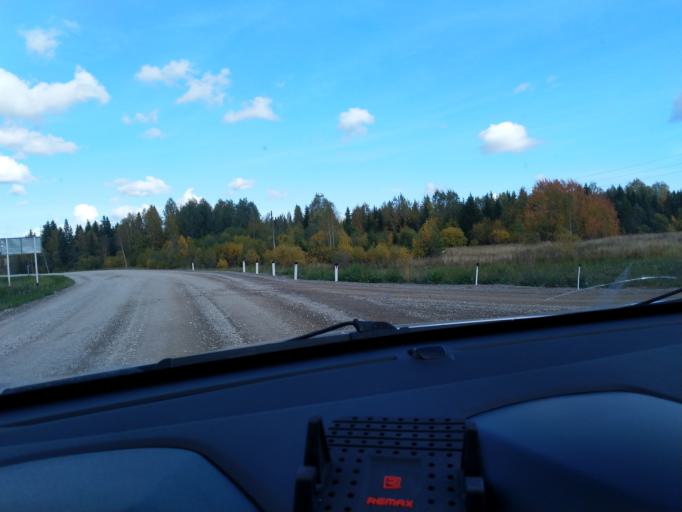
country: RU
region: Perm
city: Usol'ye
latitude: 59.4639
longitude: 56.3690
